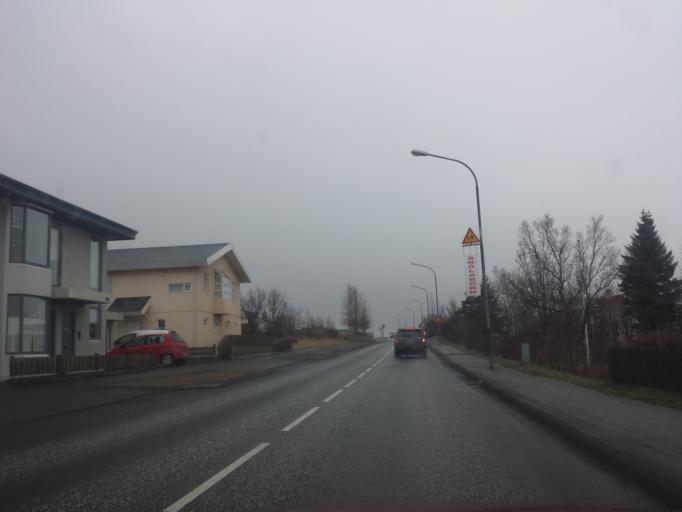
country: IS
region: Capital Region
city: Reykjavik
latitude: 64.1113
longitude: -21.8685
